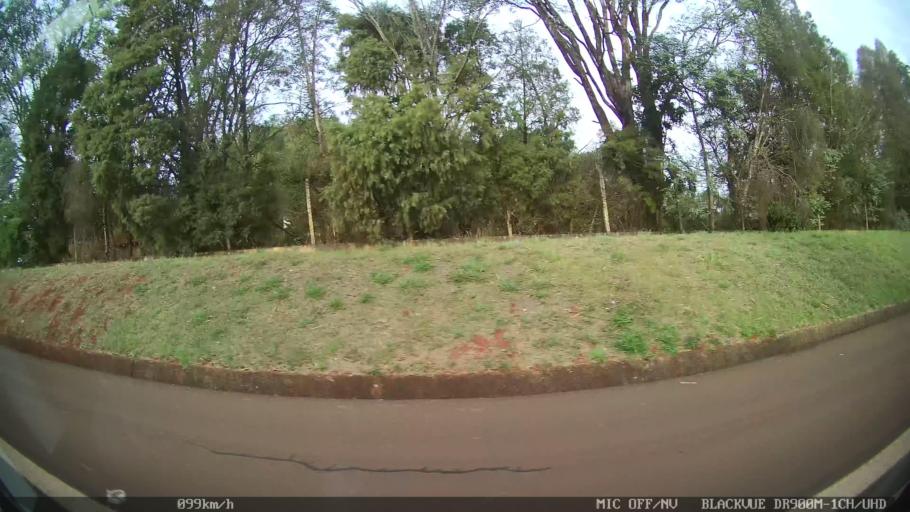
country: BR
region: Sao Paulo
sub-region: Iracemapolis
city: Iracemapolis
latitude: -22.6385
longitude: -47.5089
